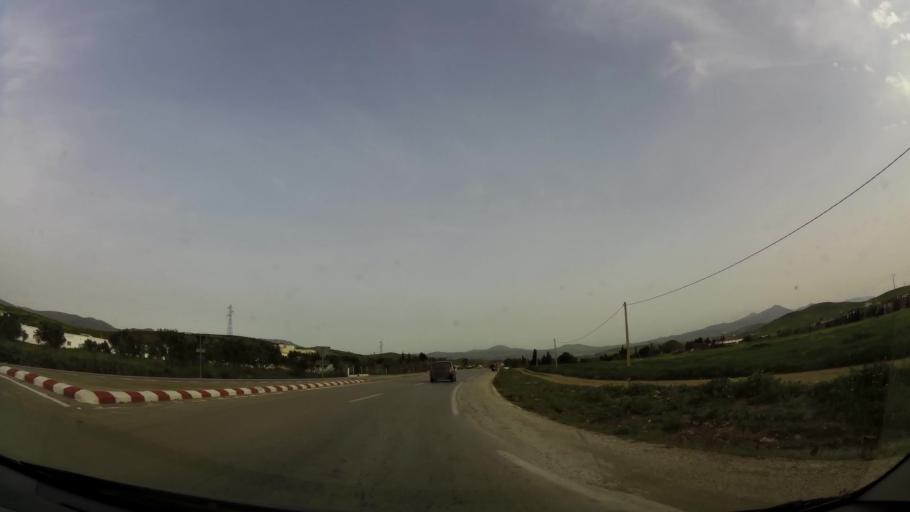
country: MA
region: Tanger-Tetouan
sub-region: Tanger-Assilah
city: Dar Chaoui
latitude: 35.6043
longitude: -5.6564
